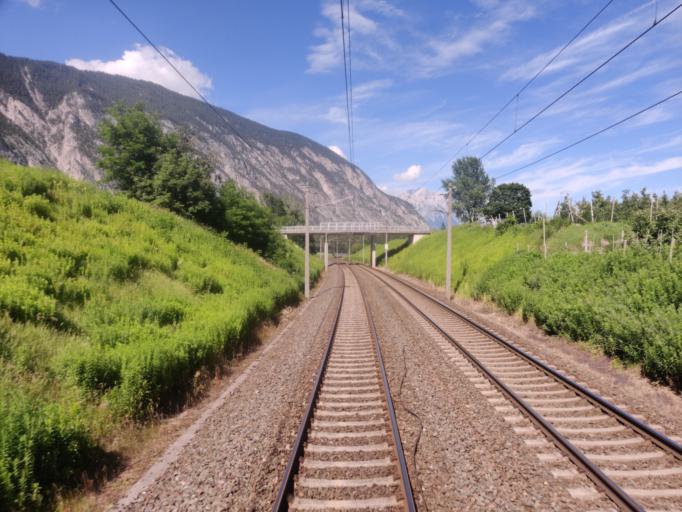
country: AT
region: Tyrol
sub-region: Politischer Bezirk Imst
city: Haiming
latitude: 47.2557
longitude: 10.8940
